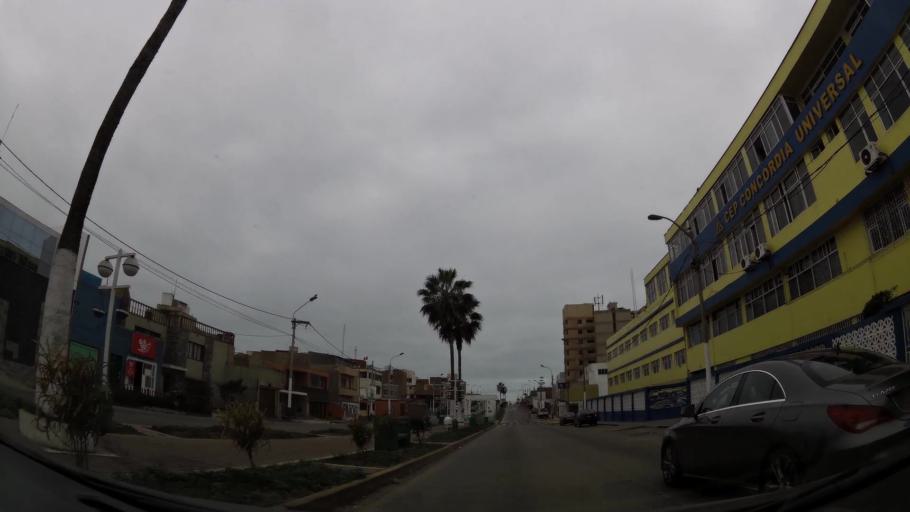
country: PE
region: Callao
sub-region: Callao
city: Callao
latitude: -12.0690
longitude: -77.1212
